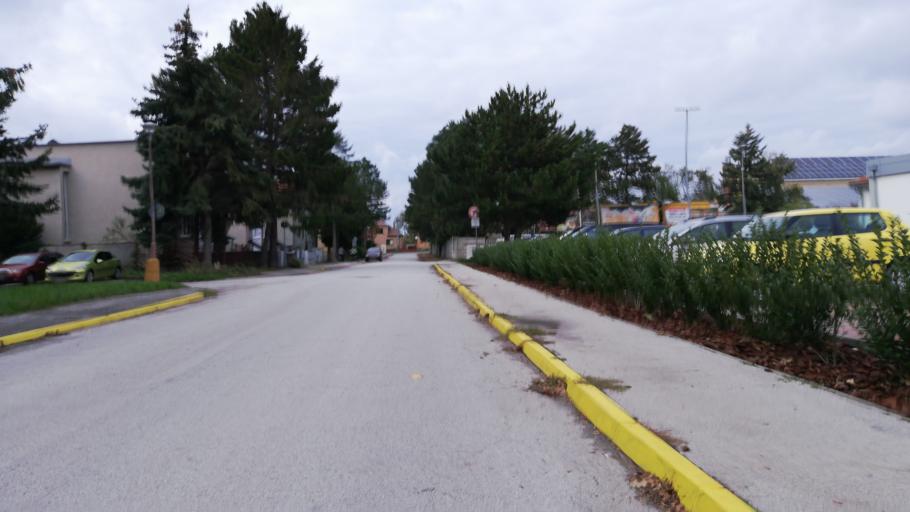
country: SK
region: Trnavsky
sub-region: Okres Skalica
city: Skalica
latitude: 48.8444
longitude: 17.2225
